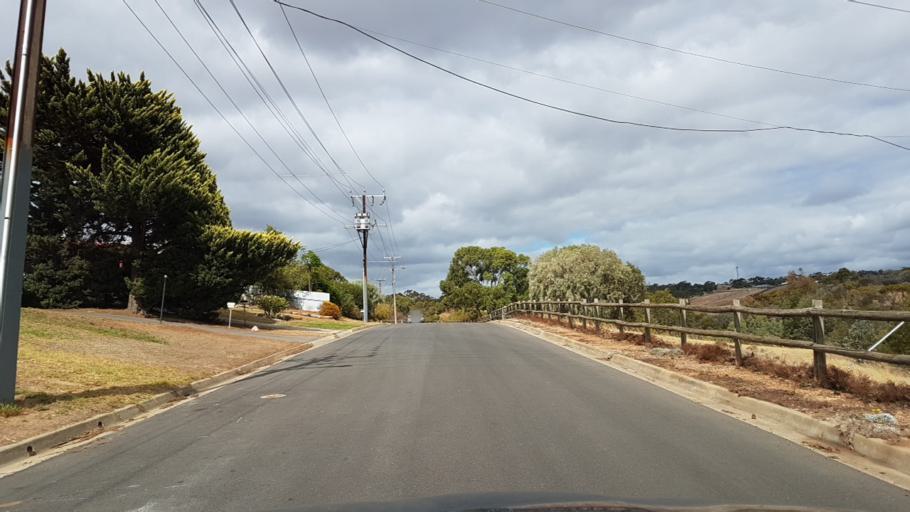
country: AU
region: South Australia
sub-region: Gawler
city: Gawler
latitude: -34.6094
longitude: 138.7531
